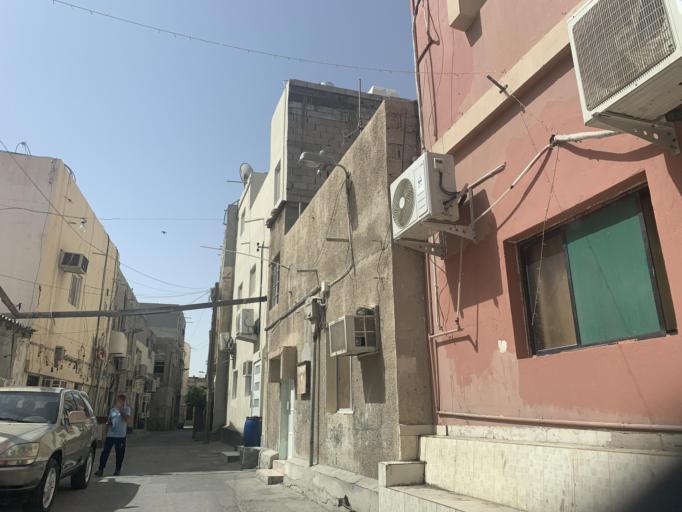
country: BH
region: Manama
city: Jidd Hafs
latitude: 26.2063
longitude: 50.5419
